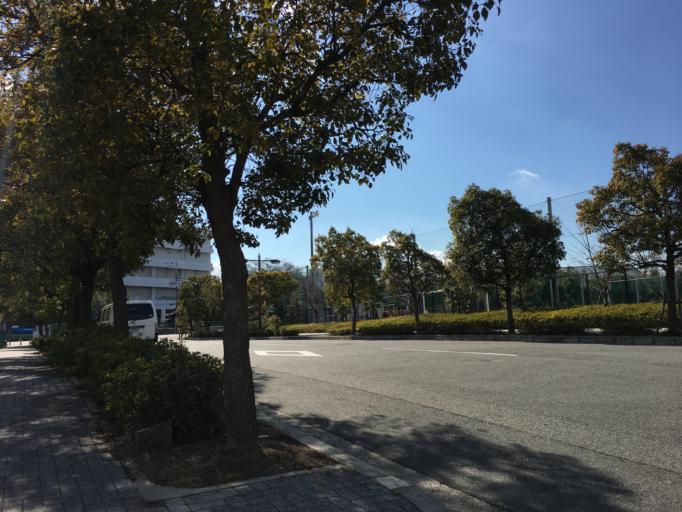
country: JP
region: Hyogo
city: Amagasaki
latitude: 34.6394
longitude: 135.4080
